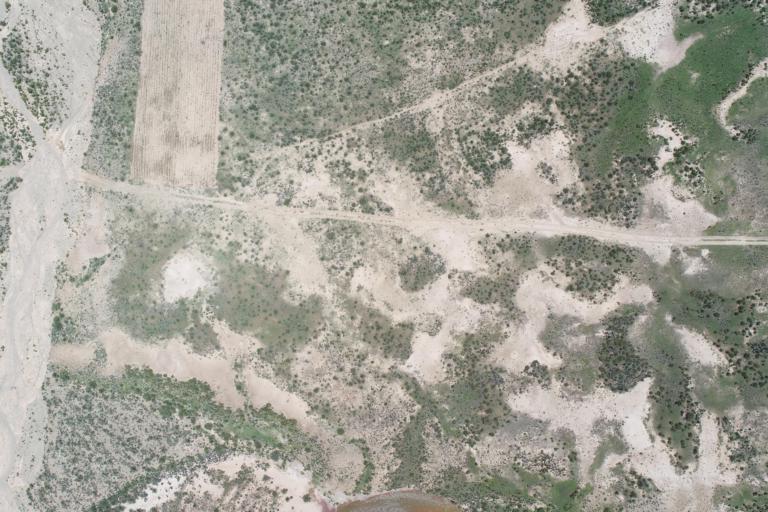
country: BO
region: La Paz
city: Curahuara de Carangas
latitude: -17.3193
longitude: -68.5093
